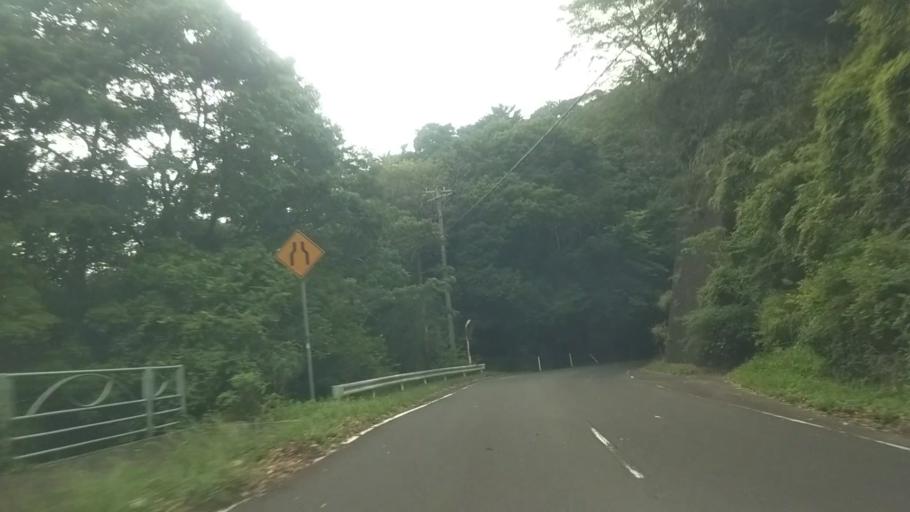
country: JP
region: Chiba
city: Kawaguchi
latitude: 35.1640
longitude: 140.1406
